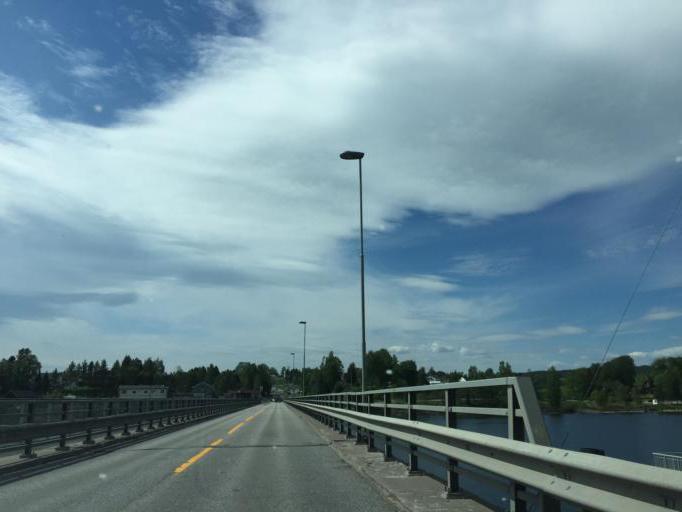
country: NO
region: Akershus
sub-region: Nes
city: Arnes
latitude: 60.1554
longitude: 11.4196
